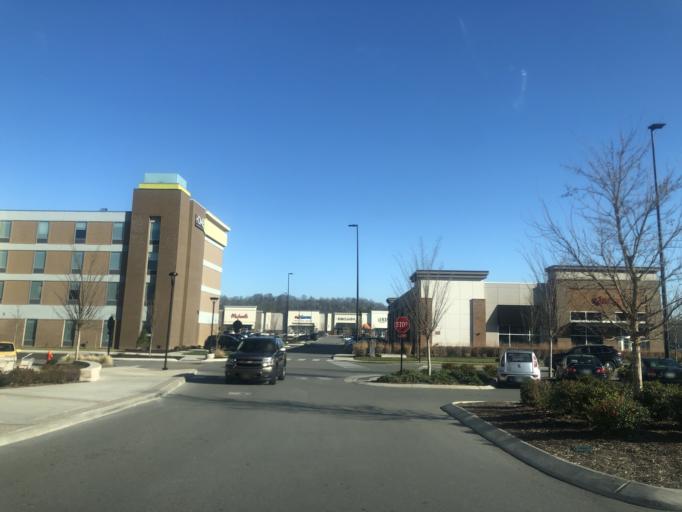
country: US
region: Tennessee
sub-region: Davidson County
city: Belle Meade
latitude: 36.0797
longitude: -86.9488
